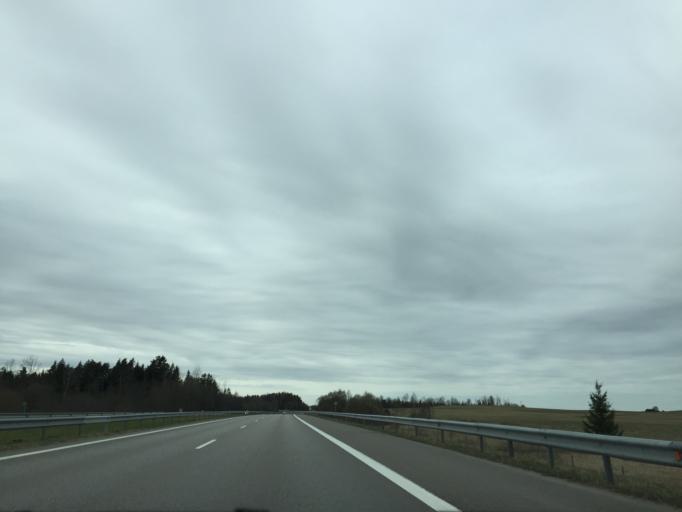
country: LT
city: Rietavas
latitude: 55.6666
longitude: 21.7376
